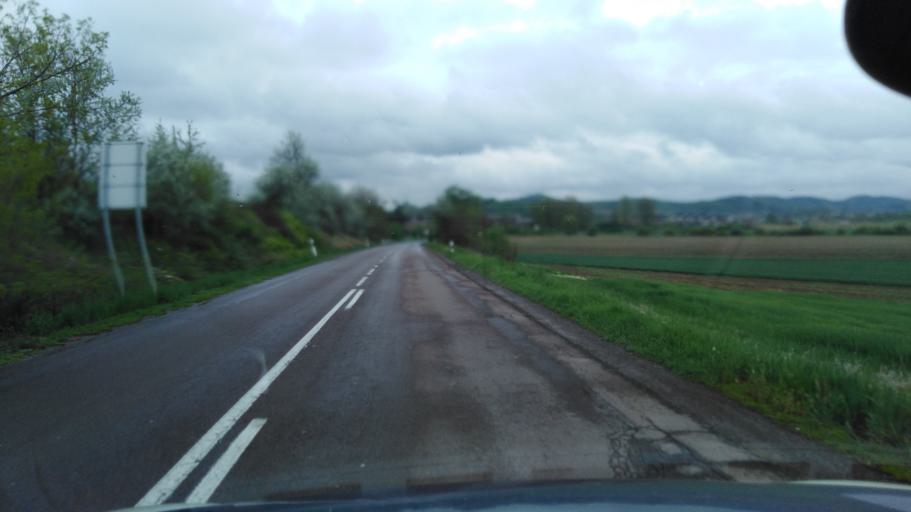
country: HU
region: Nograd
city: Karancskeszi
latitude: 48.1196
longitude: 19.6451
